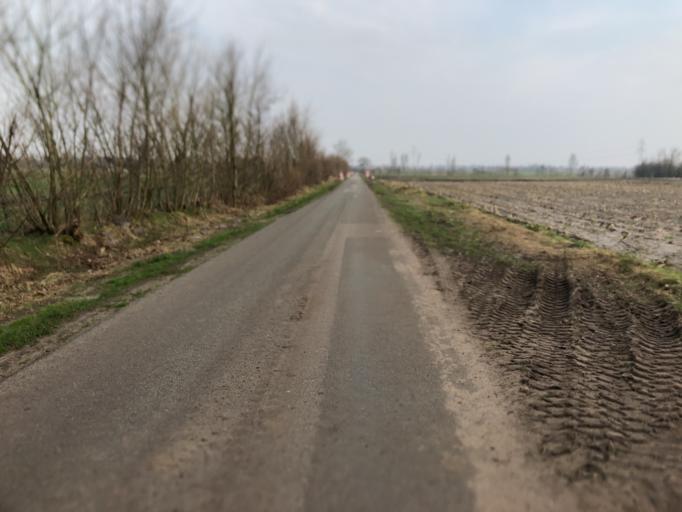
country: DE
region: Schleswig-Holstein
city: Wanderup
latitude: 54.6968
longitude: 9.3645
